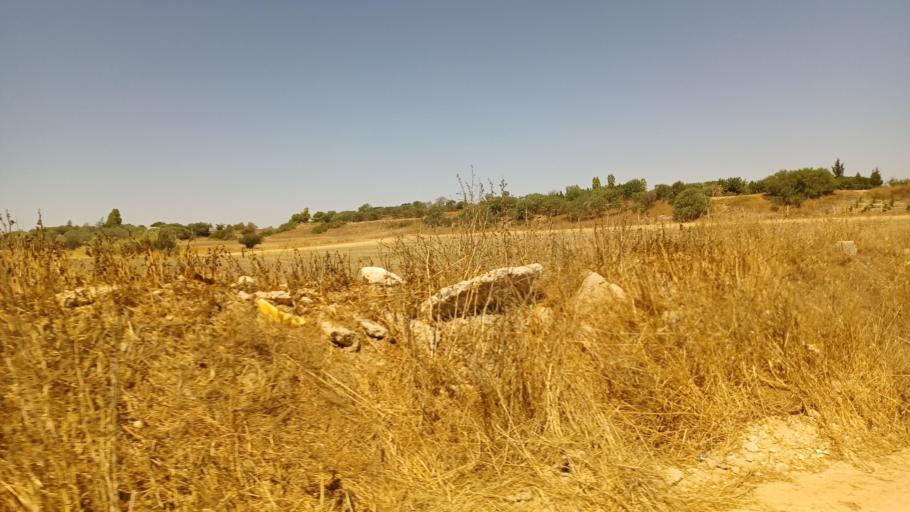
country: CY
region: Ammochostos
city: Avgorou
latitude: 35.0522
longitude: 33.8323
